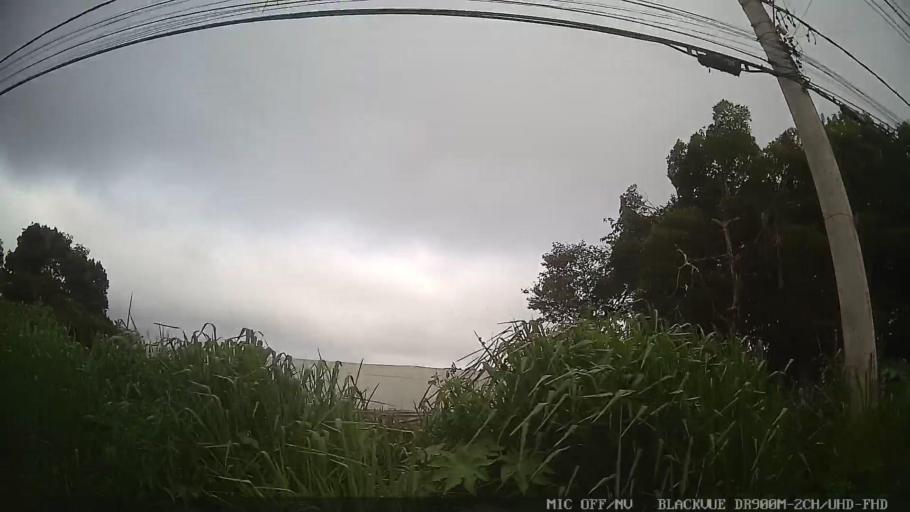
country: BR
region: Sao Paulo
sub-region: Biritiba-Mirim
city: Biritiba Mirim
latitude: -23.5643
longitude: -46.0856
